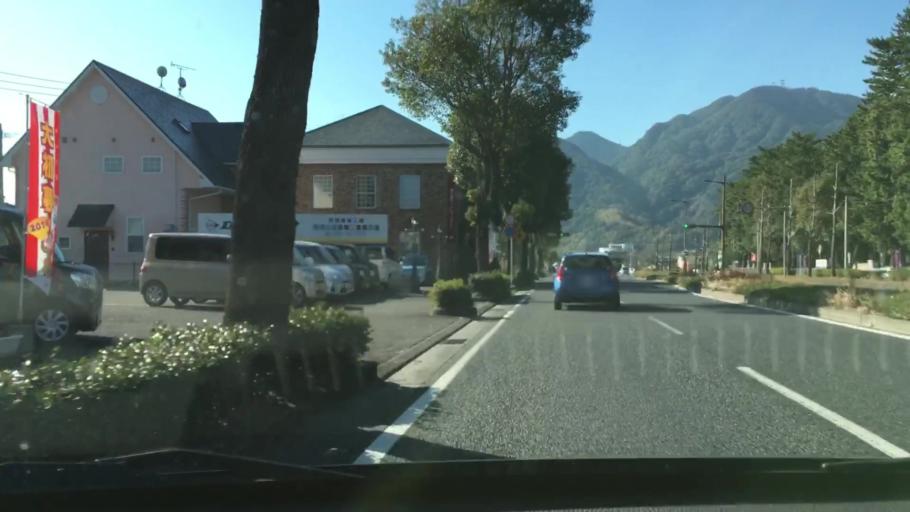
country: JP
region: Kagoshima
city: Kajiki
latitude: 31.7141
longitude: 130.6179
